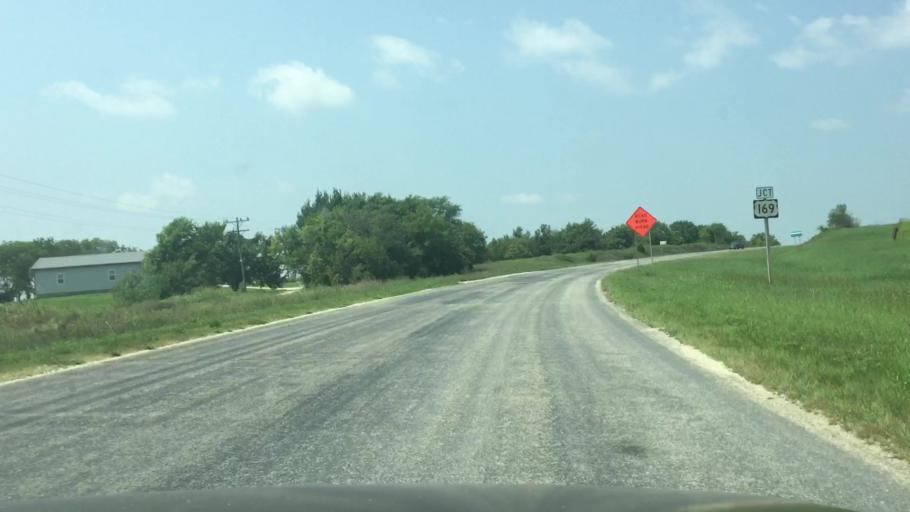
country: US
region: Kansas
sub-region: Allen County
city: Iola
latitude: 37.8786
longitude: -95.3922
